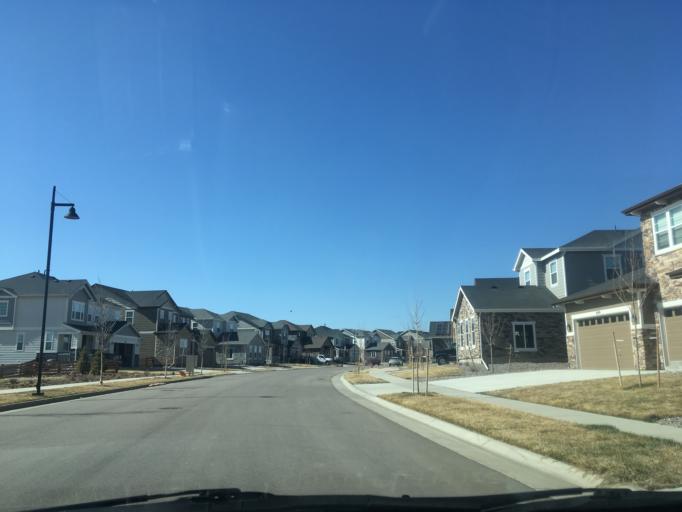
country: US
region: Colorado
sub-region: Boulder County
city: Erie
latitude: 40.0554
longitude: -105.0285
